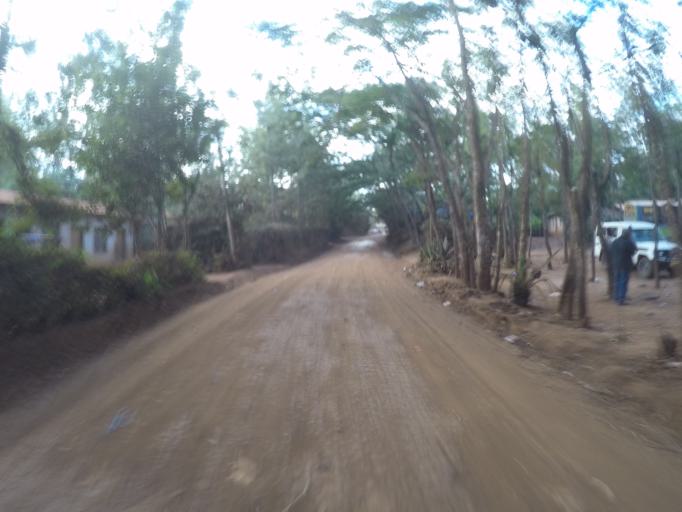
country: TZ
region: Arusha
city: Kiratu
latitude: -3.3353
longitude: 35.6667
